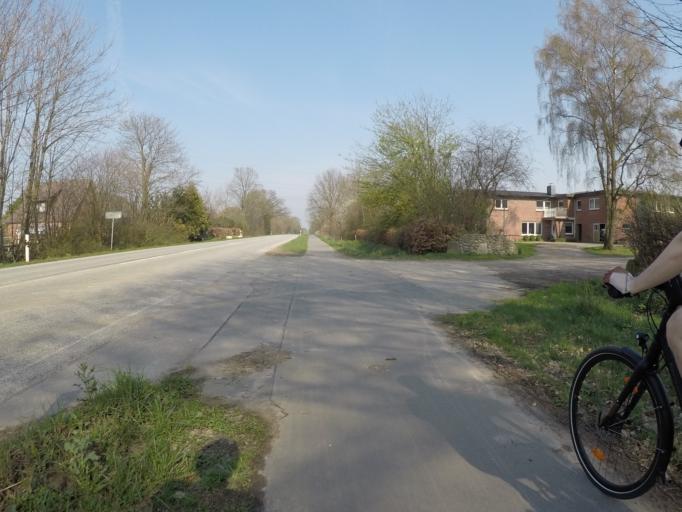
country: DE
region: Schleswig-Holstein
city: Seth
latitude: 53.8321
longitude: 10.2117
